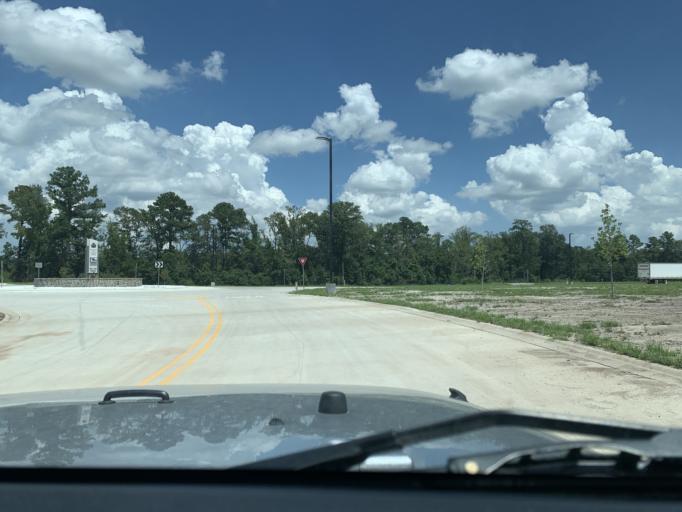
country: US
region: Georgia
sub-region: Chatham County
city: Bloomingdale
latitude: 32.1174
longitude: -81.2781
